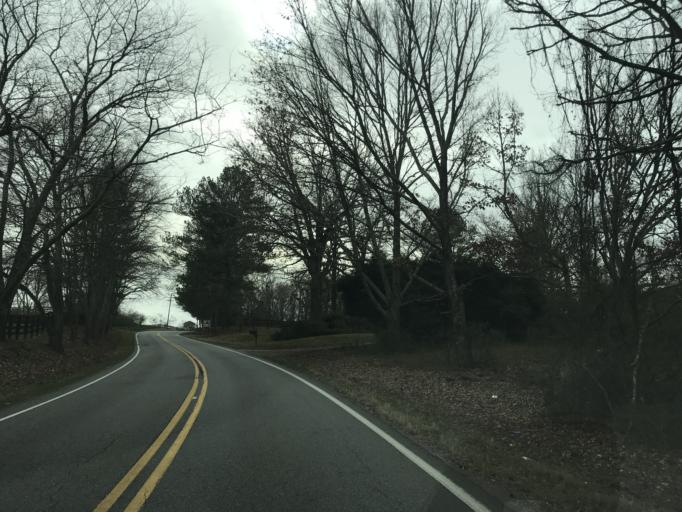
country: US
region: Georgia
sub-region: Fulton County
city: Milton
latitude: 34.1899
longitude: -84.3416
